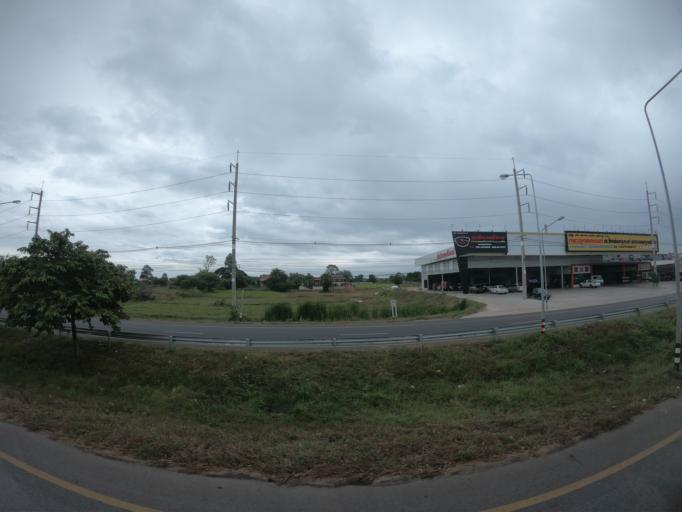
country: TH
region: Roi Et
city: Roi Et
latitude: 16.0509
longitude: 103.6206
